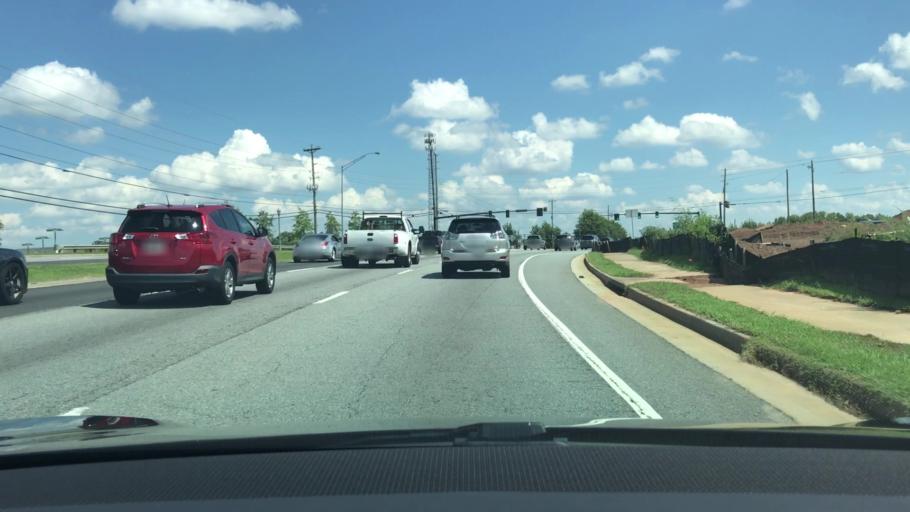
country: US
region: Georgia
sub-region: Gwinnett County
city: Buford
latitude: 34.0840
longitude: -83.9890
